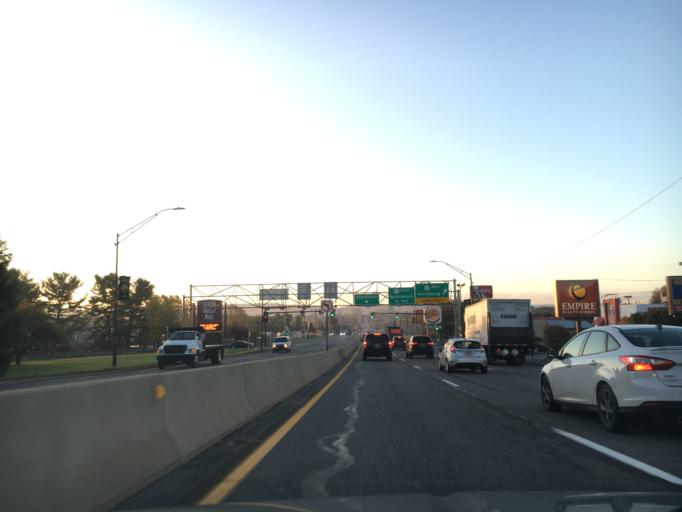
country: US
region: Pennsylvania
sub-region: Lehigh County
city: Fullerton
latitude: 40.6305
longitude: -75.4851
